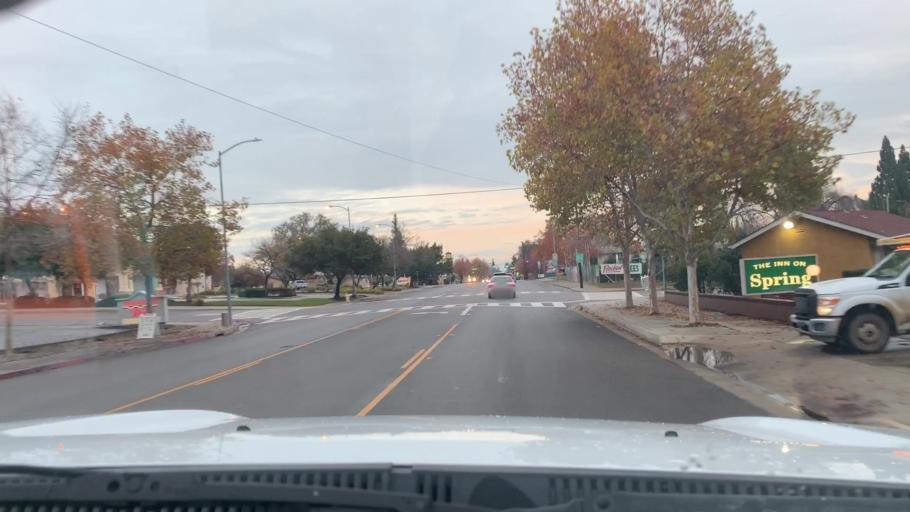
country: US
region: California
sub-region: San Luis Obispo County
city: Paso Robles
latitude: 35.6221
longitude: -120.6910
